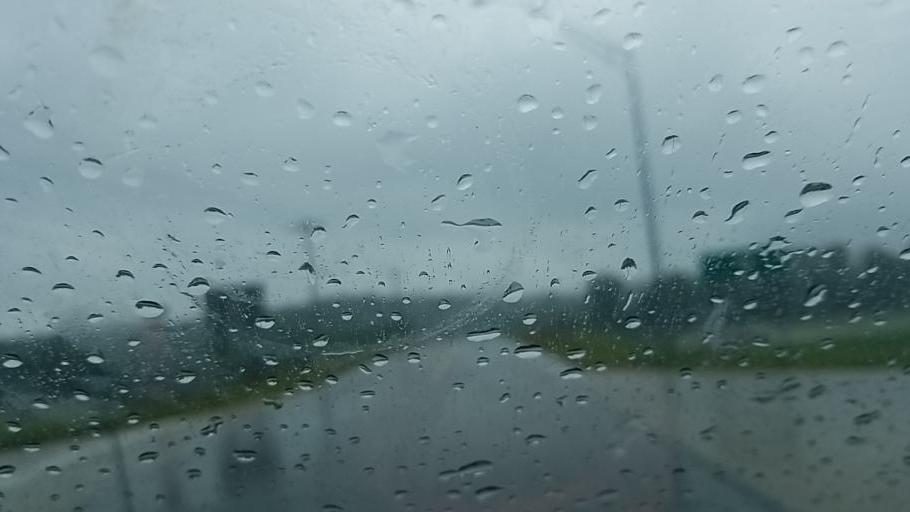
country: US
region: Ohio
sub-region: Logan County
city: Bellefontaine
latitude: 40.3238
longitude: -83.6636
